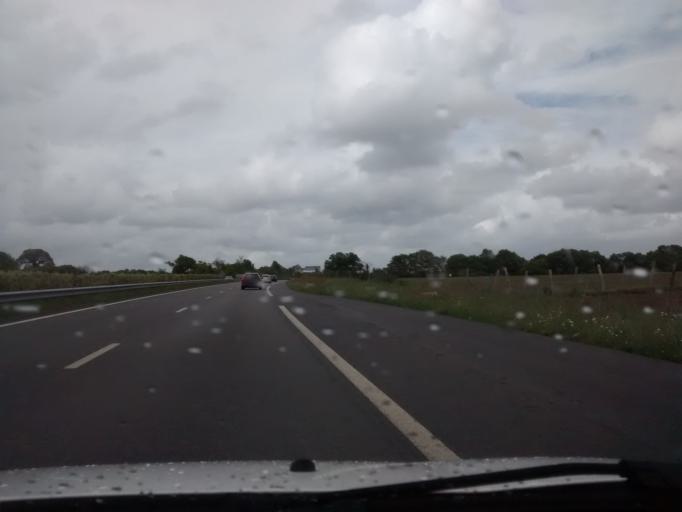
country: FR
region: Brittany
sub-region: Departement du Morbihan
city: Trefflean
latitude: 47.7072
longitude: -2.6172
